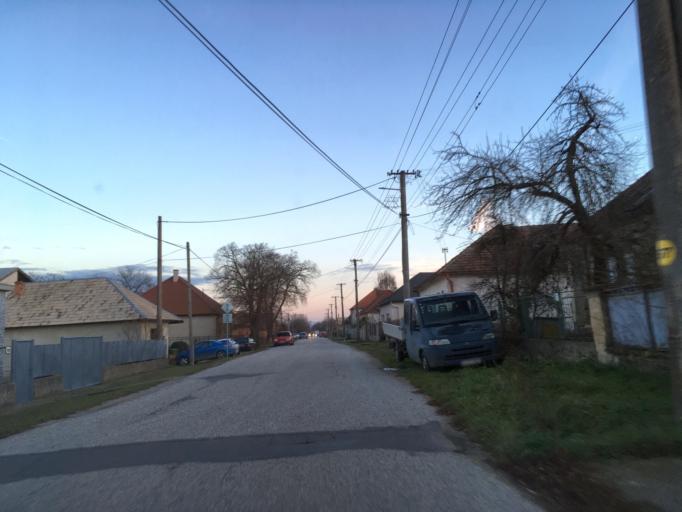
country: SK
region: Nitriansky
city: Svodin
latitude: 47.8677
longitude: 18.4673
